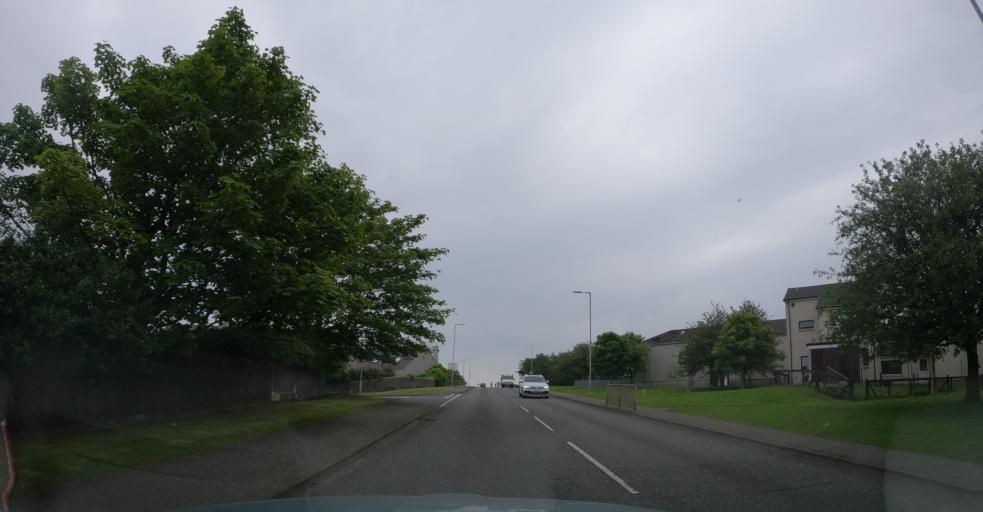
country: GB
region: Scotland
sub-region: Eilean Siar
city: Isle of Lewis
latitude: 58.2227
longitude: -6.3860
